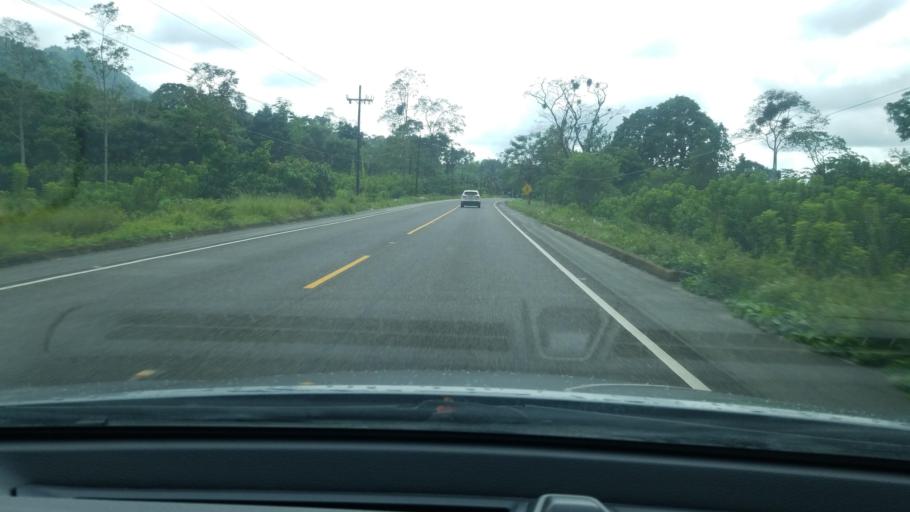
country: HN
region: Cortes
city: Potrerillos
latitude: 15.6123
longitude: -88.2823
